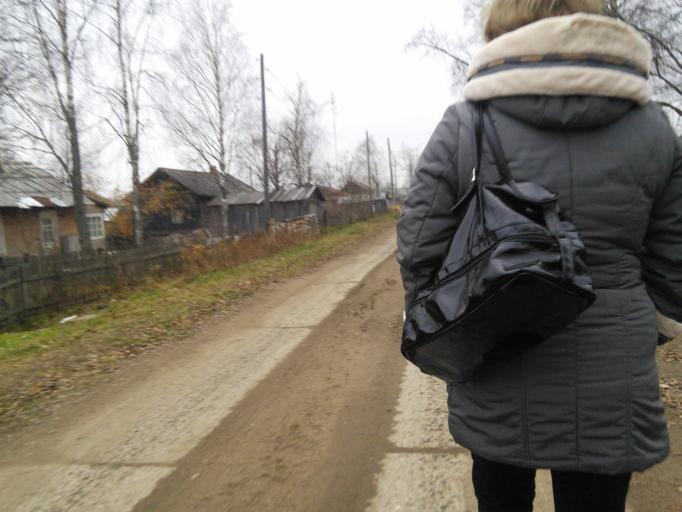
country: RU
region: Vologda
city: Kharovsk
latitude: 59.8084
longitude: 40.1749
